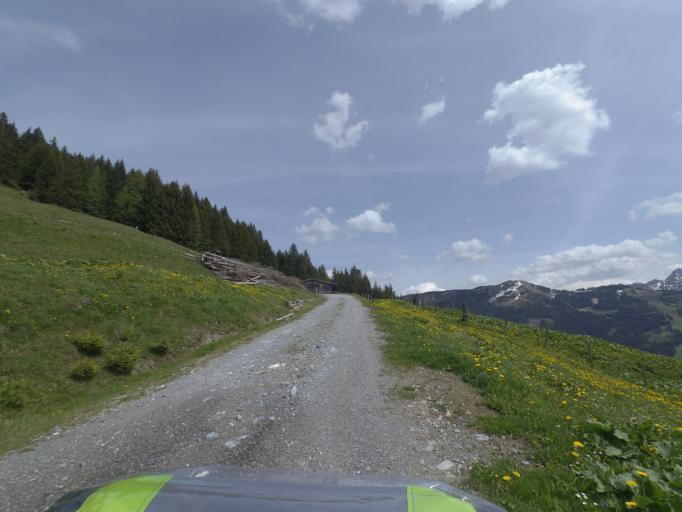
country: AT
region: Salzburg
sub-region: Politischer Bezirk Sankt Johann im Pongau
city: Dorfgastein
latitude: 47.2625
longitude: 13.1196
